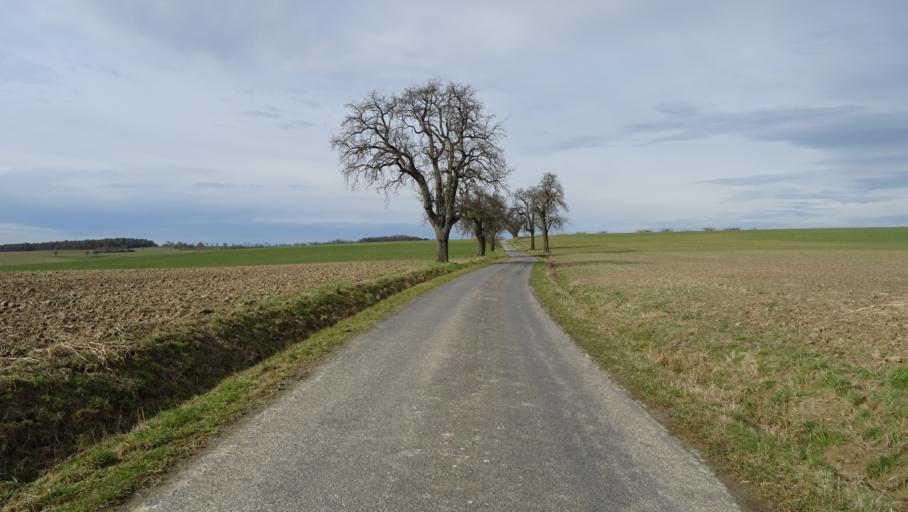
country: DE
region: Baden-Wuerttemberg
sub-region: Karlsruhe Region
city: Seckach
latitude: 49.4249
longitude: 9.2762
